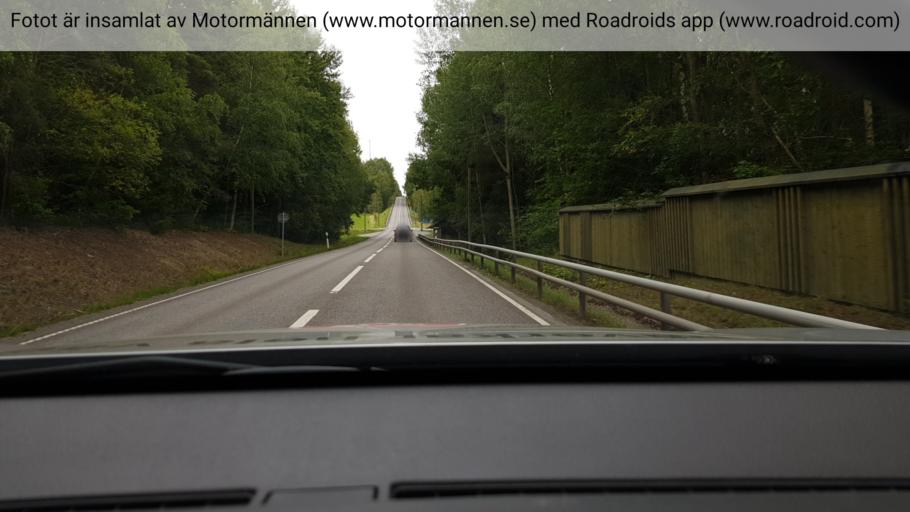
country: SE
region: Soedermanland
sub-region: Gnesta Kommun
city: Gnesta
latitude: 59.0351
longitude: 17.3445
